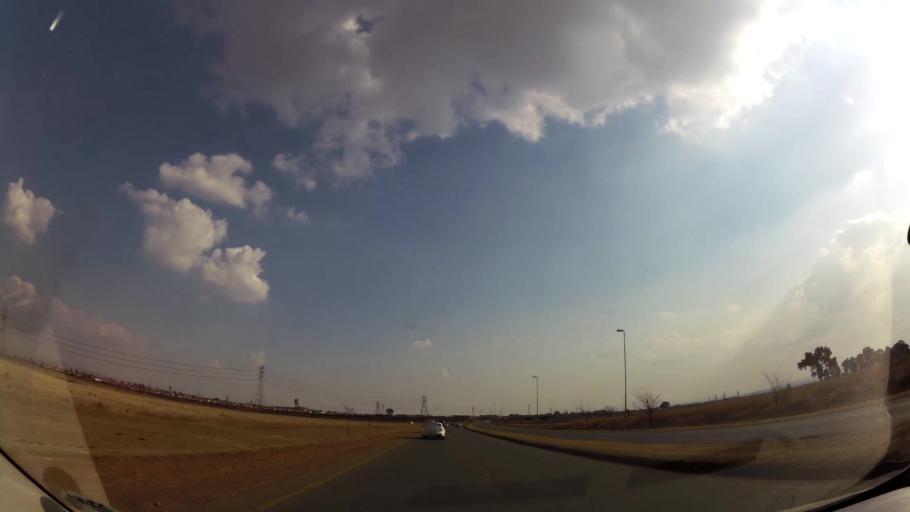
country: ZA
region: Gauteng
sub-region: Ekurhuleni Metropolitan Municipality
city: Germiston
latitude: -26.3385
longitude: 28.2265
